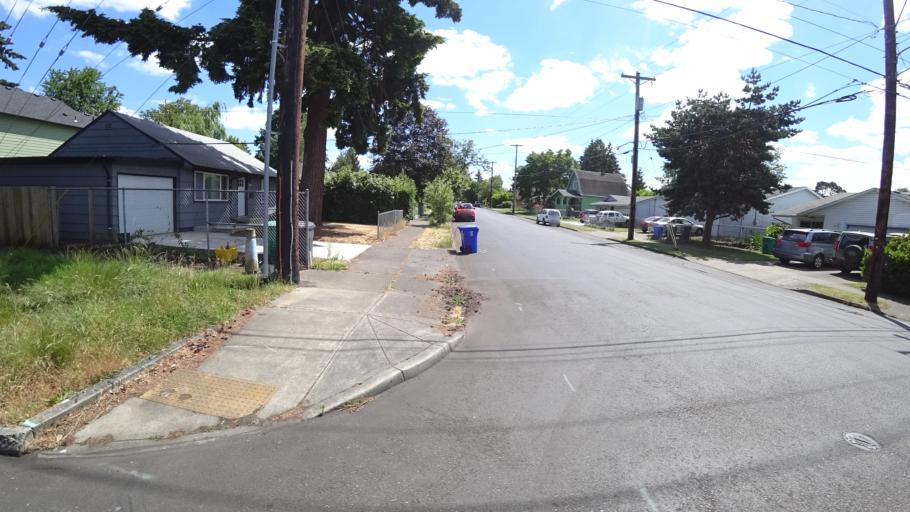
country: US
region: Oregon
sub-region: Multnomah County
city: Portland
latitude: 45.5866
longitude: -122.7134
